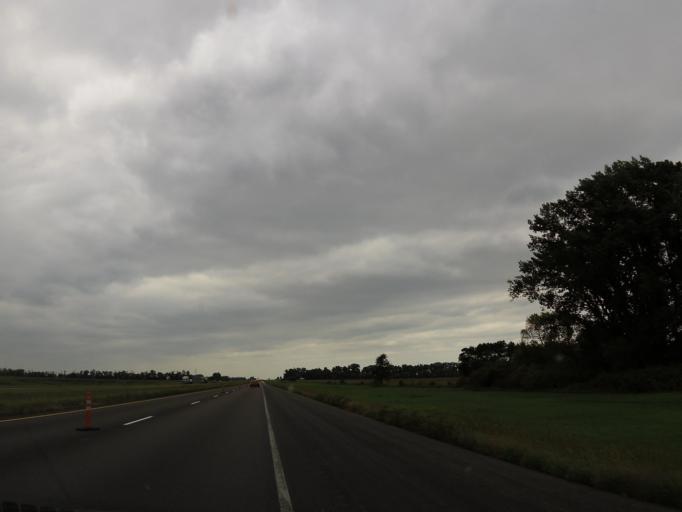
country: US
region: North Dakota
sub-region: Richland County
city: Wahpeton
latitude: 46.0867
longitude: -96.8356
